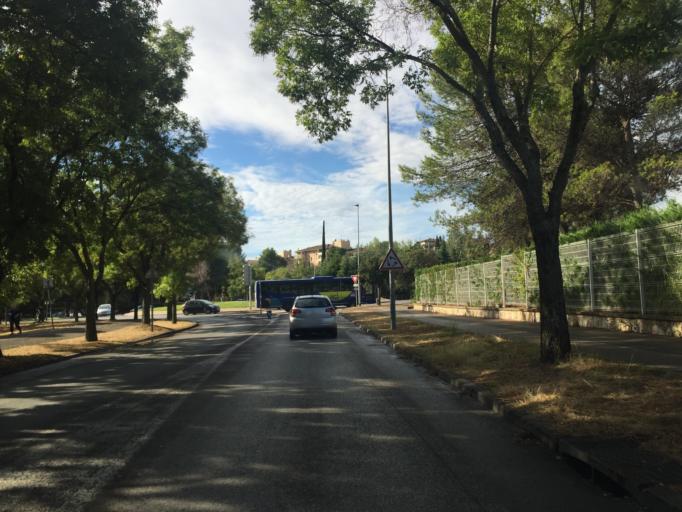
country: FR
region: Provence-Alpes-Cote d'Azur
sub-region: Departement des Bouches-du-Rhone
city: Aix-en-Provence
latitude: 43.5258
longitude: 5.4237
